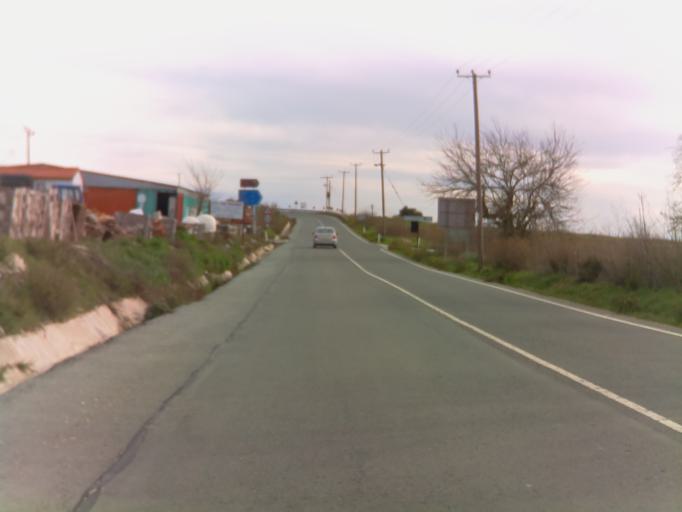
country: CY
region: Pafos
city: Pegeia
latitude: 34.9377
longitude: 32.4120
